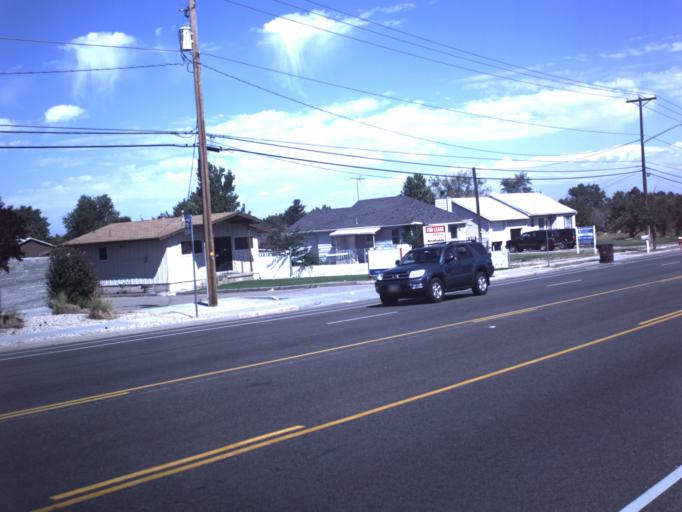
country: US
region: Utah
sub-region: Weber County
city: Roy
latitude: 41.1796
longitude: -112.0259
